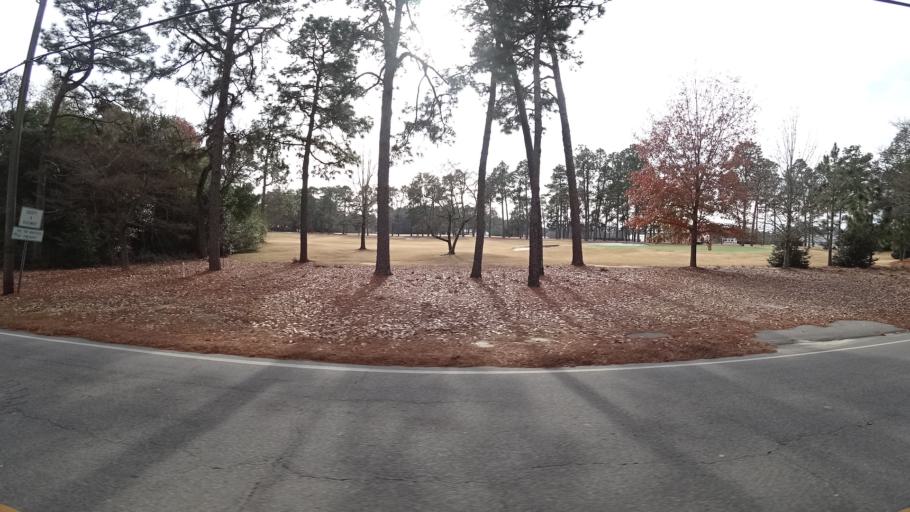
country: US
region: North Carolina
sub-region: Moore County
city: Pinehurst
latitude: 35.1837
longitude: -79.4629
